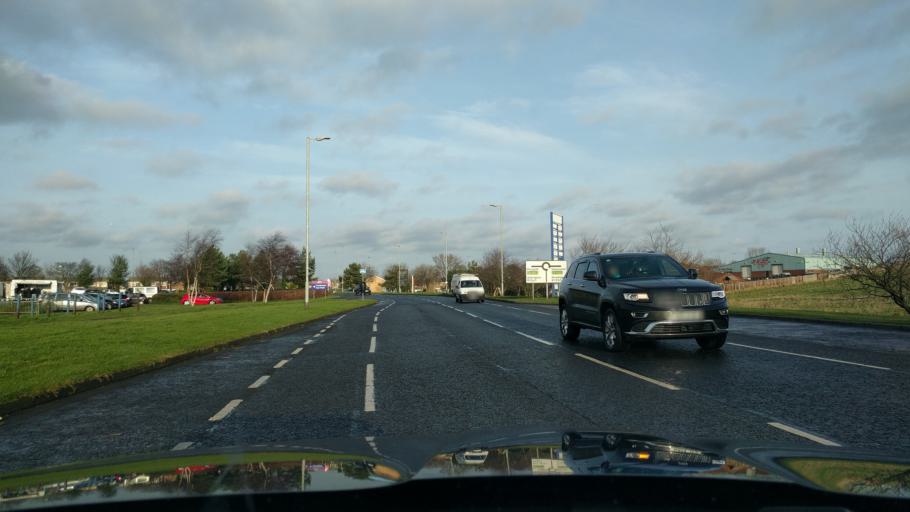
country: GB
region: England
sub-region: Northumberland
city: Ashington
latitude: 55.1691
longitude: -1.5493
